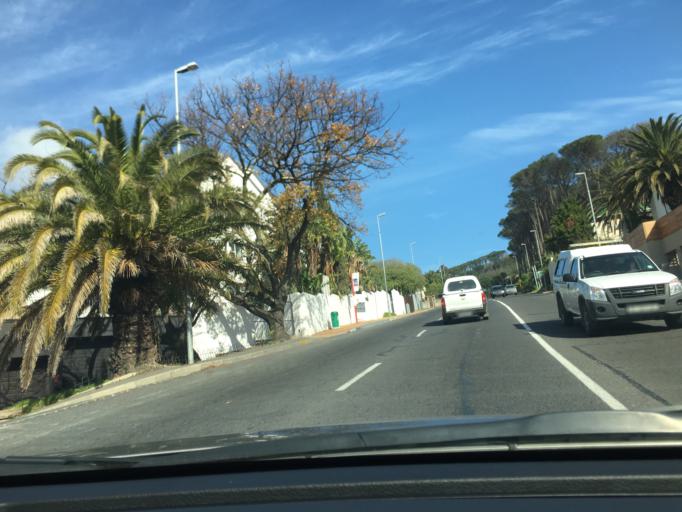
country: ZA
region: Western Cape
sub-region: City of Cape Town
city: Cape Town
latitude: -33.9351
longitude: 18.4021
